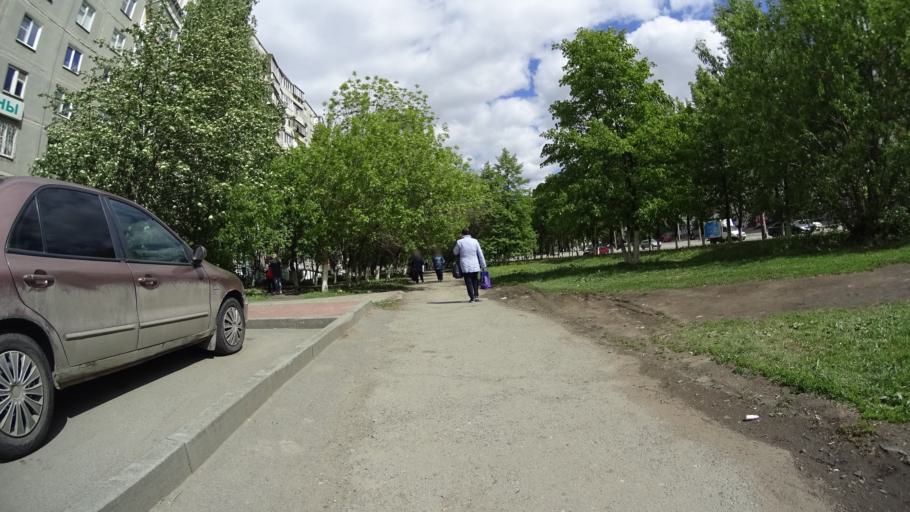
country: RU
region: Chelyabinsk
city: Roshchino
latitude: 55.1947
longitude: 61.3039
